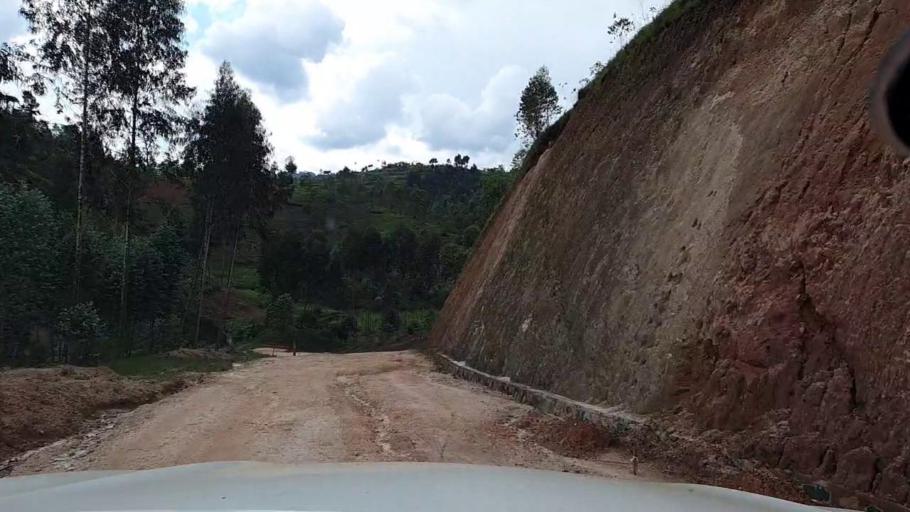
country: RW
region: Southern Province
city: Nzega
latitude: -2.6959
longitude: 29.4414
